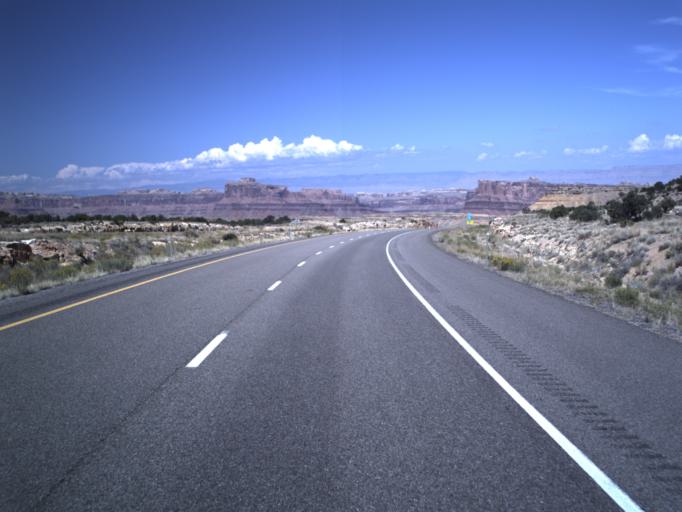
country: US
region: Utah
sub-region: Emery County
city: Castle Dale
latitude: 38.9201
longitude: -110.5008
